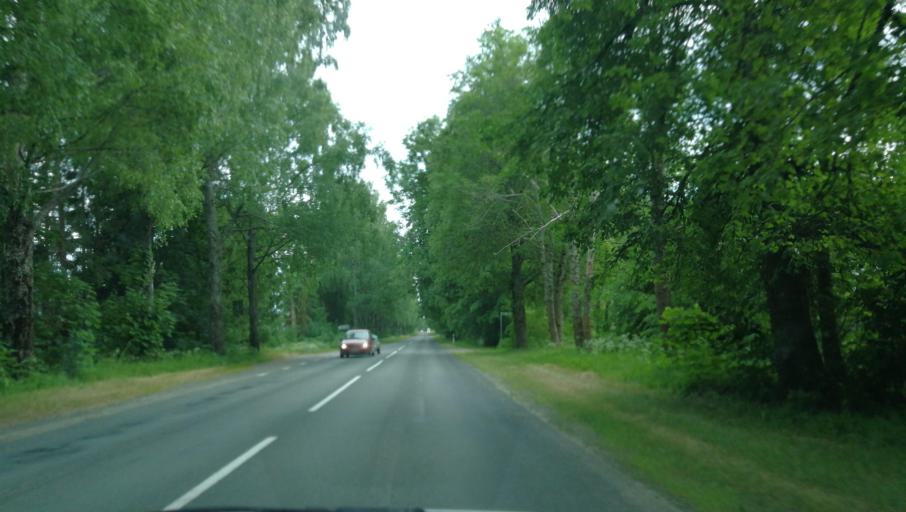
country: LV
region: Valmieras Rajons
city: Valmiera
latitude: 57.6766
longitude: 25.4300
